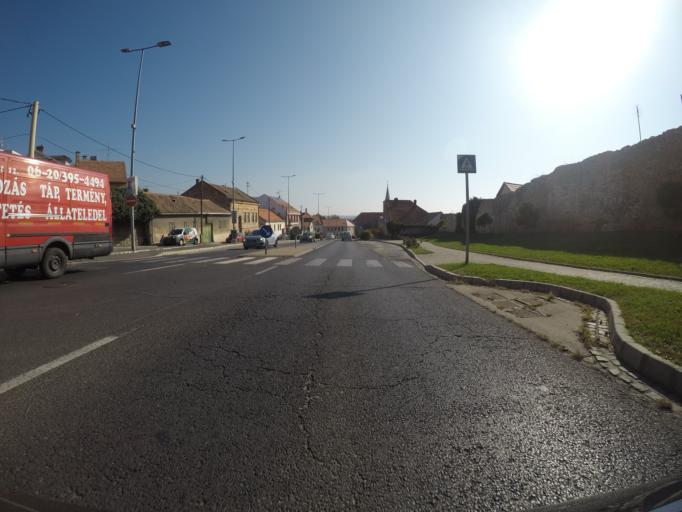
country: HU
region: Baranya
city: Pecs
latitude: 46.0804
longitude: 18.2332
